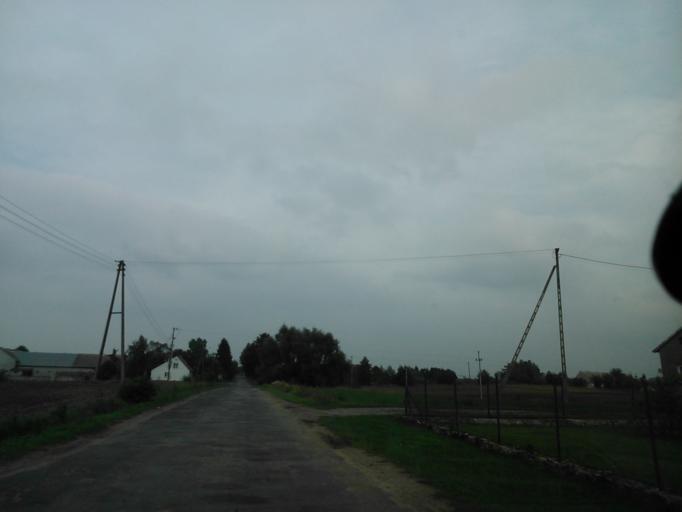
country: PL
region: Kujawsko-Pomorskie
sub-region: Powiat wabrzeski
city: Pluznica
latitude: 53.2516
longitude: 18.8259
